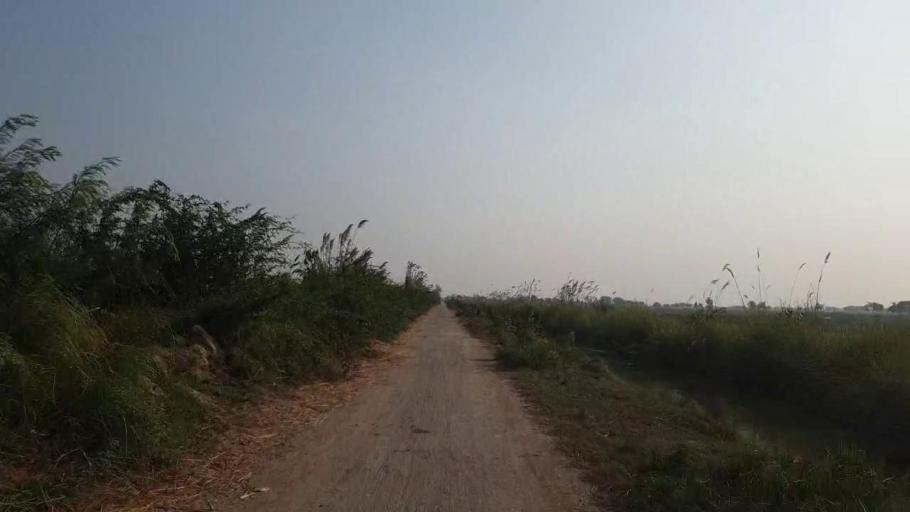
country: PK
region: Sindh
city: Tando Muhammad Khan
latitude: 25.0949
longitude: 68.3558
